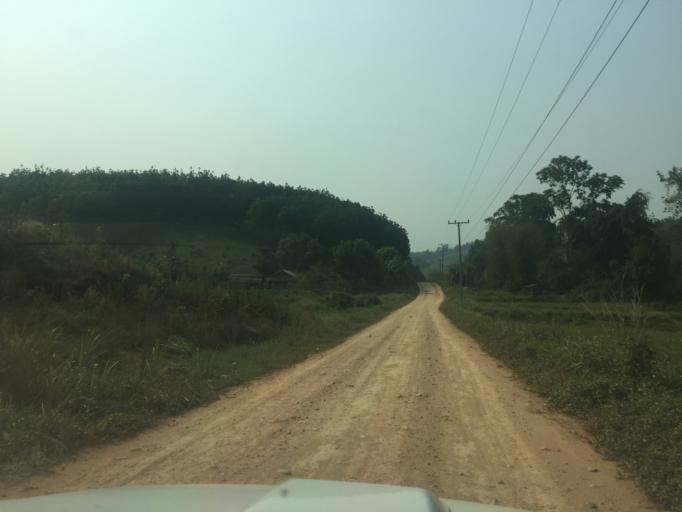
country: TH
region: Phayao
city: Phu Sang
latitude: 19.6435
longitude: 100.5237
